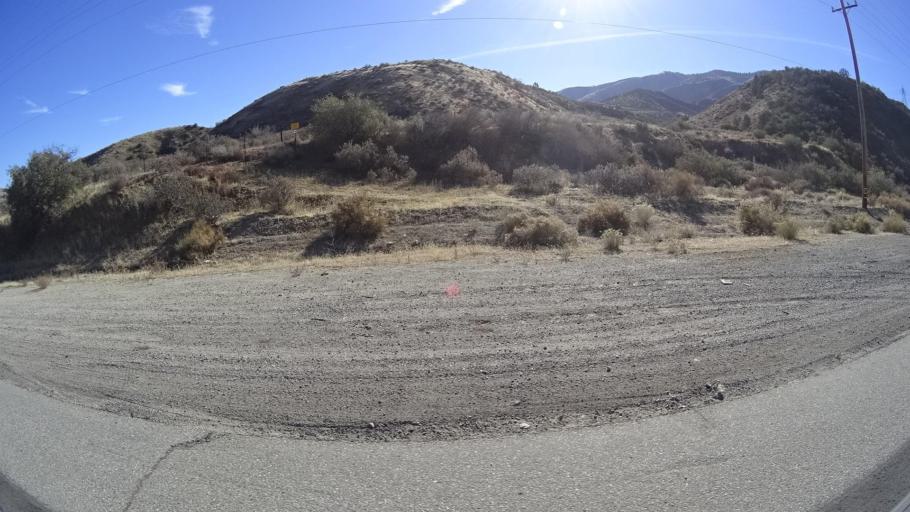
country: US
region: California
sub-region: Kern County
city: Lebec
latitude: 34.8181
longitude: -118.9010
